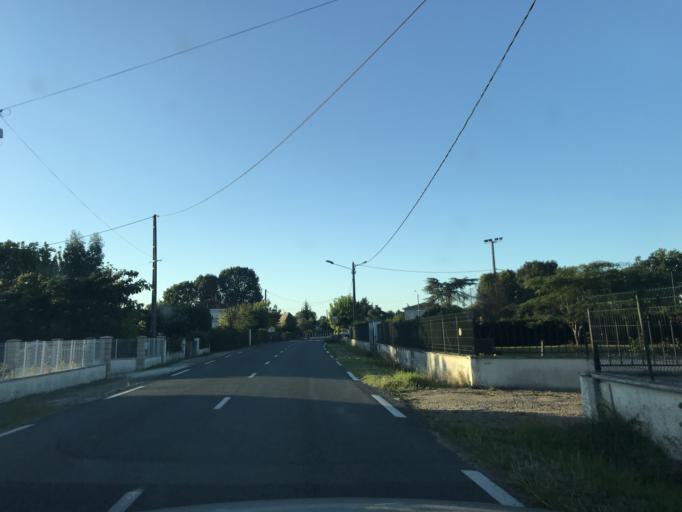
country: FR
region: Aquitaine
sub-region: Departement de la Gironde
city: Saint-Medard-de-Guizieres
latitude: 45.0109
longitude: -0.0537
